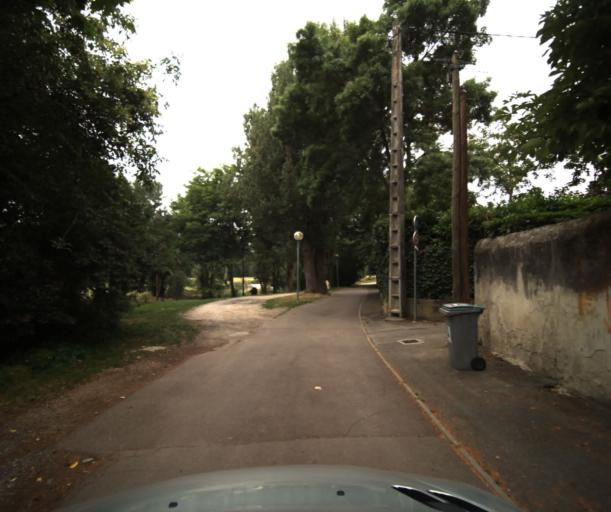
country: FR
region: Midi-Pyrenees
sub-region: Departement de la Haute-Garonne
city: Portet-sur-Garonne
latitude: 43.5195
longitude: 1.4064
